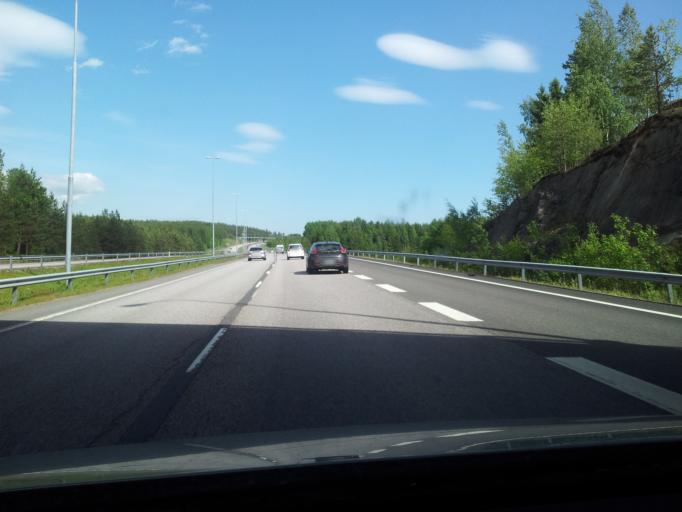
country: FI
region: Uusimaa
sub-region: Loviisa
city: Perna
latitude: 60.4913
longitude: 25.9589
